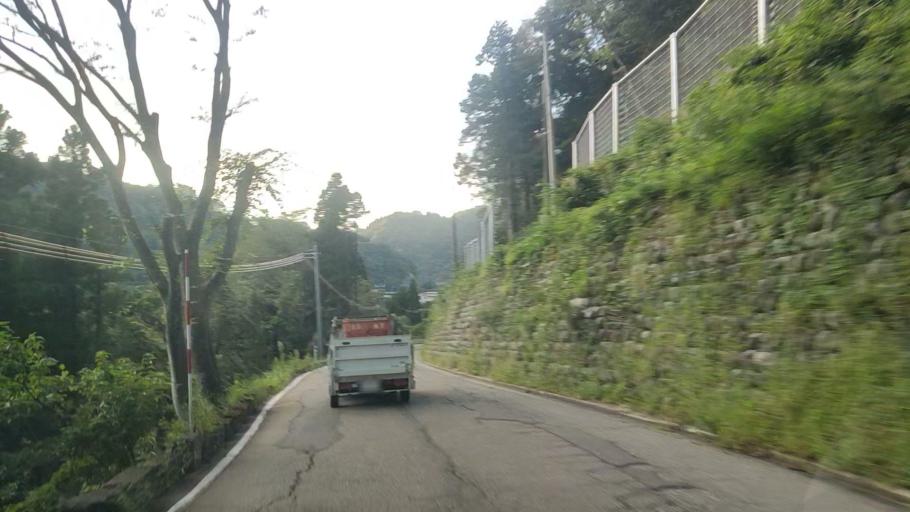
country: JP
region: Toyama
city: Nanto-shi
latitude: 36.5583
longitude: 137.0088
